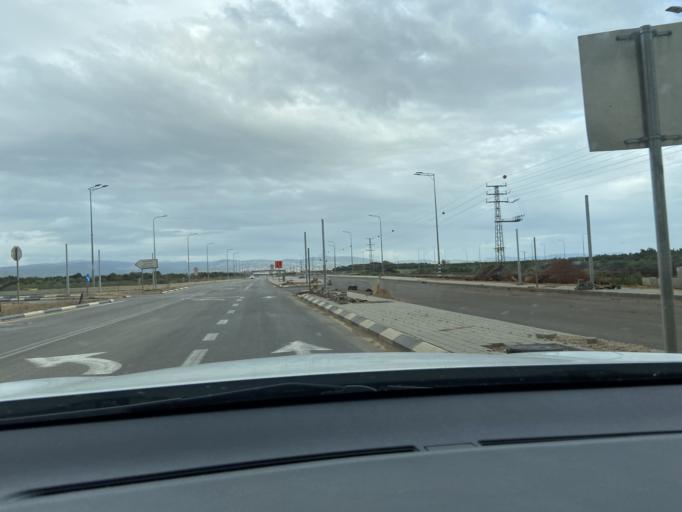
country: IL
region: Northern District
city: El Mazra`a
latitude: 32.9797
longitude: 35.1061
